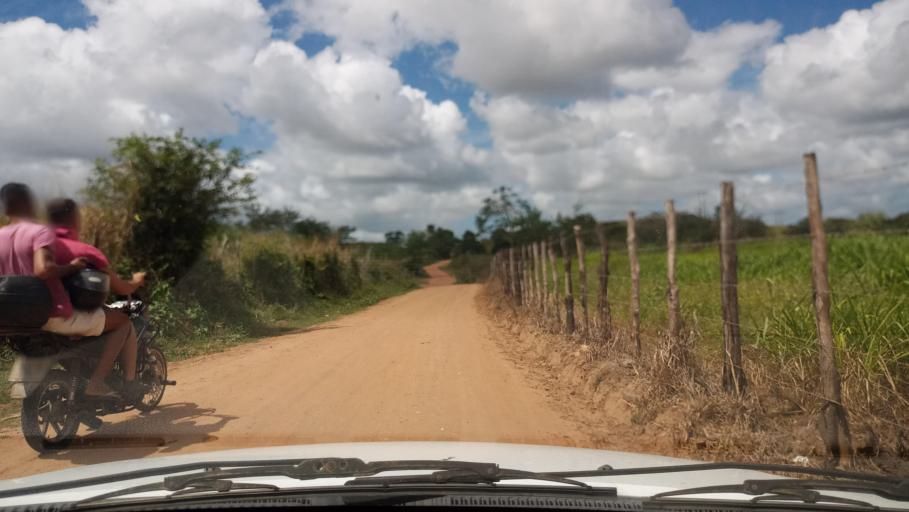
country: BR
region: Rio Grande do Norte
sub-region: Goianinha
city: Goianinha
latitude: -6.2621
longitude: -35.2411
